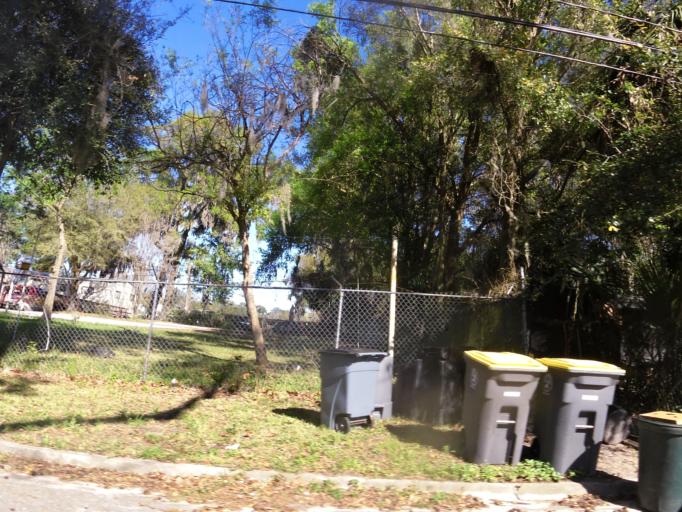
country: US
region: Florida
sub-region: Duval County
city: Jacksonville
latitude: 30.3616
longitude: -81.6515
